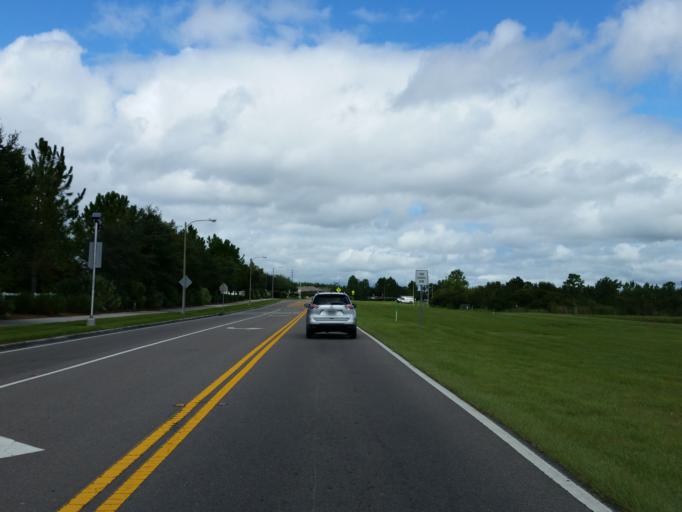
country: US
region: Florida
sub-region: Pasco County
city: Wesley Chapel
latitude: 28.2114
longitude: -82.3001
